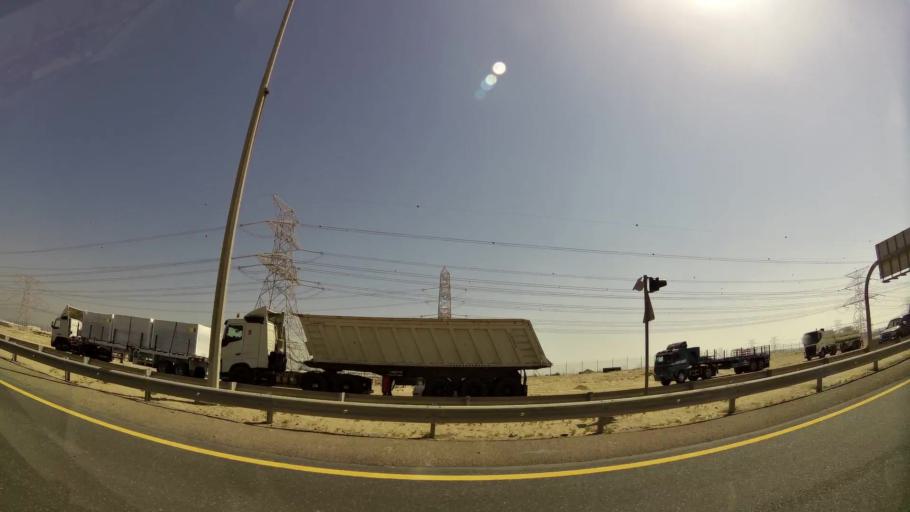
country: AE
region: Dubai
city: Dubai
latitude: 24.9357
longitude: 55.0782
